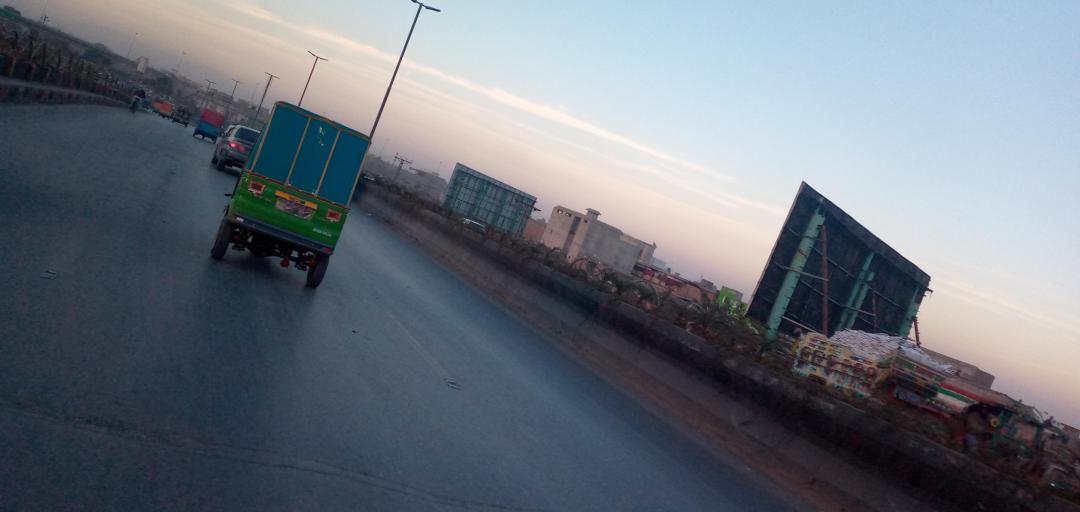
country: PK
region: Khyber Pakhtunkhwa
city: Peshawar
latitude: 34.0198
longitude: 71.6217
